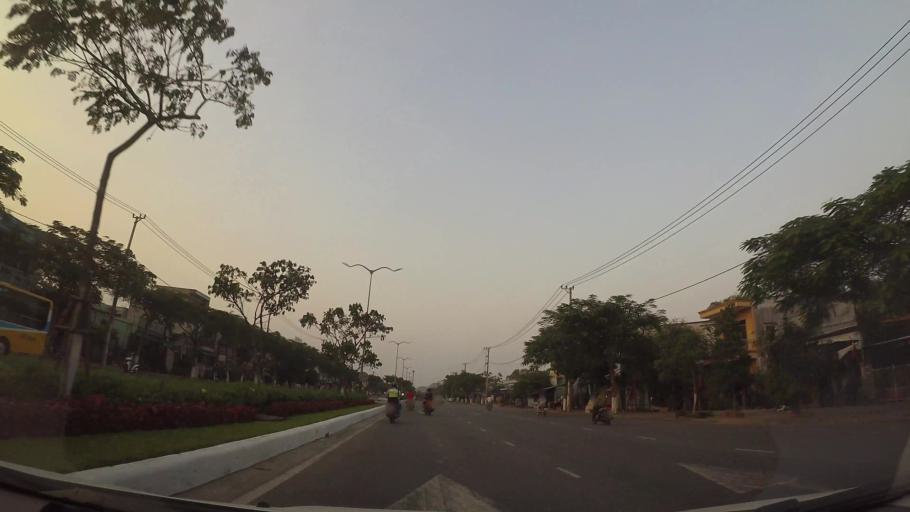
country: VN
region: Da Nang
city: Ngu Hanh Son
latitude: 15.9803
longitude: 108.2555
